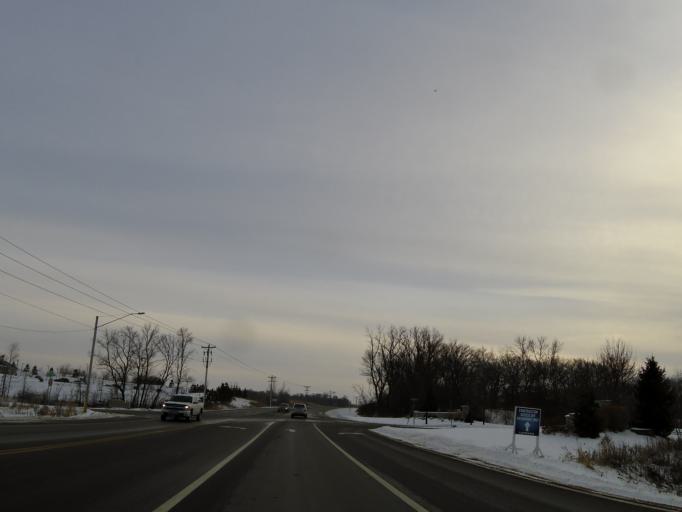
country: US
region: Minnesota
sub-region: Carver County
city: Victoria
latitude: 44.8385
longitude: -93.6523
